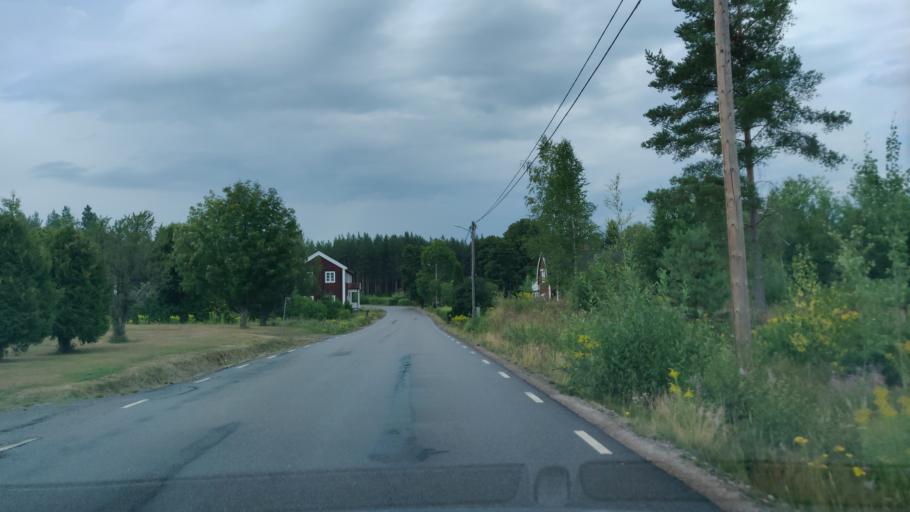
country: SE
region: Vaermland
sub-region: Munkfors Kommun
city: Munkfors
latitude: 59.8655
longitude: 13.5448
